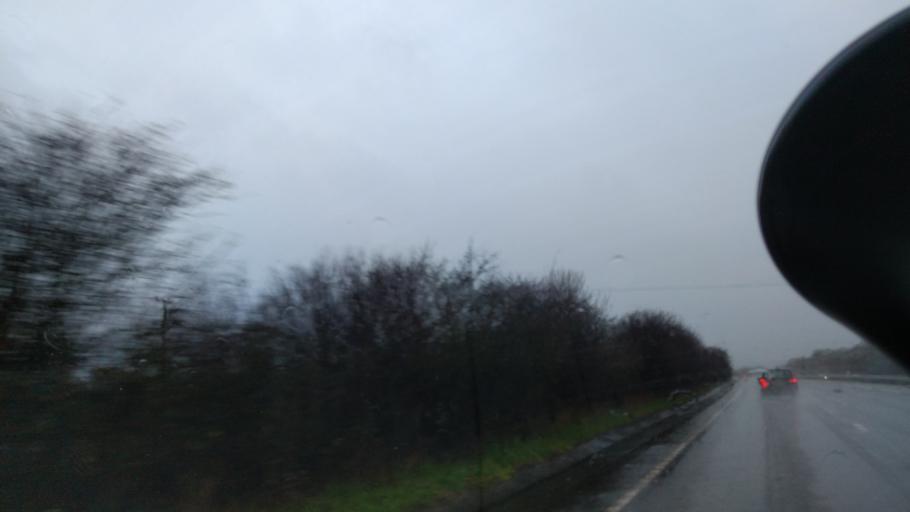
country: GB
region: England
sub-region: West Sussex
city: Rustington
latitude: 50.8399
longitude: -0.4683
